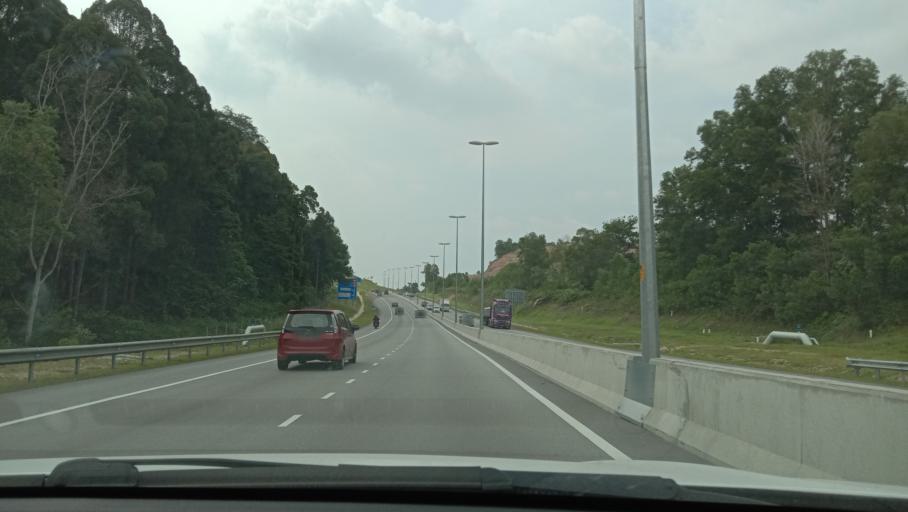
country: MY
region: Selangor
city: Kampung Baru Subang
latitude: 3.1284
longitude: 101.5100
